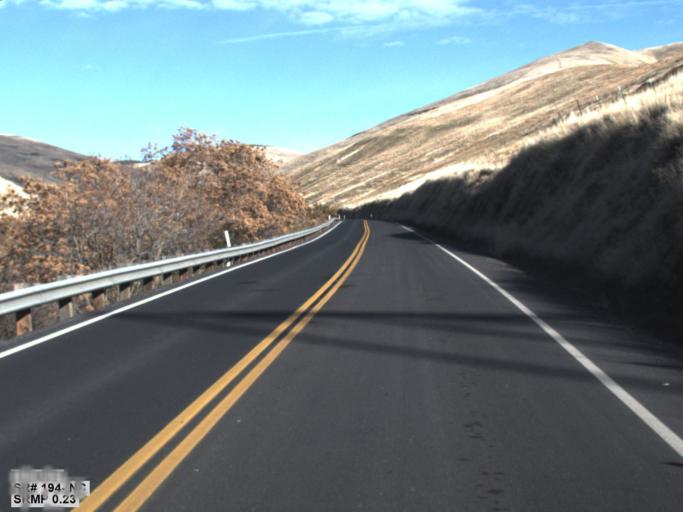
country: US
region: Washington
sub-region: Whitman County
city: Colfax
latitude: 46.7055
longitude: -117.4666
